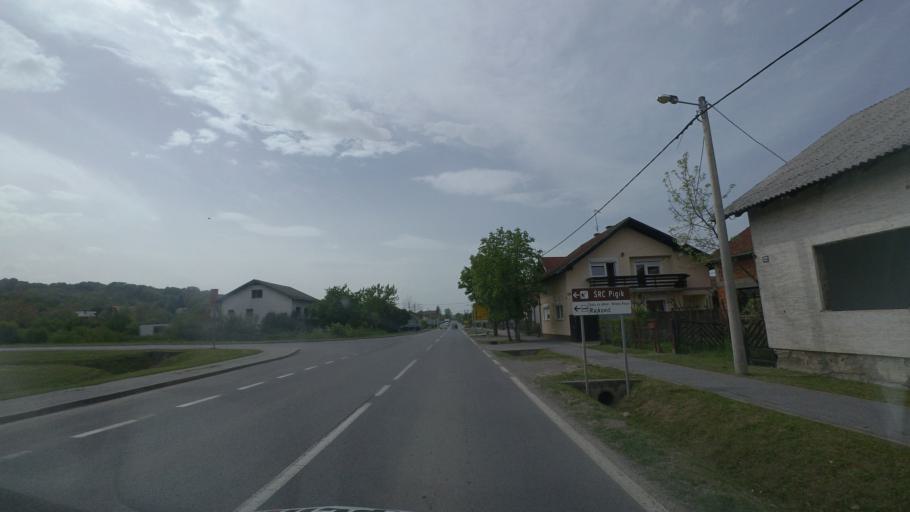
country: HR
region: Sisacko-Moslavacka
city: Petrinja
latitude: 45.4382
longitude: 16.2610
